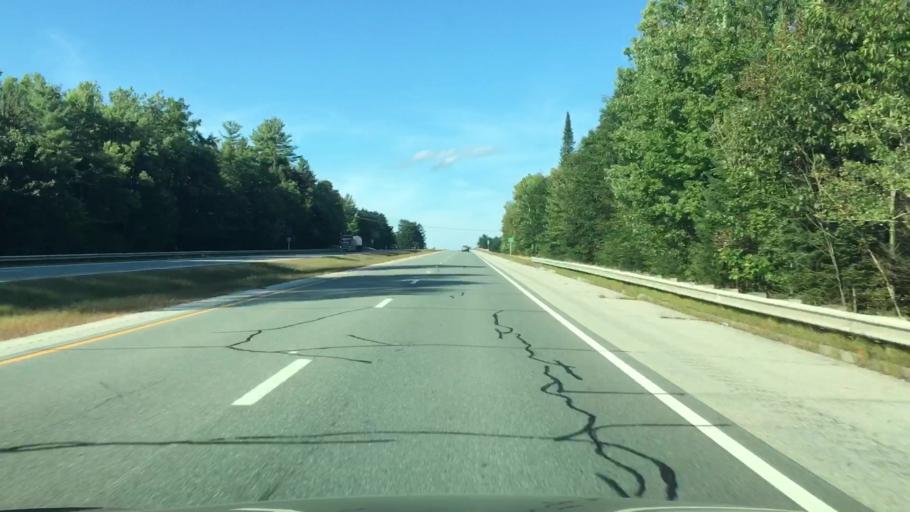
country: US
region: New Hampshire
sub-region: Grafton County
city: Littleton
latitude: 44.2552
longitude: -71.7568
